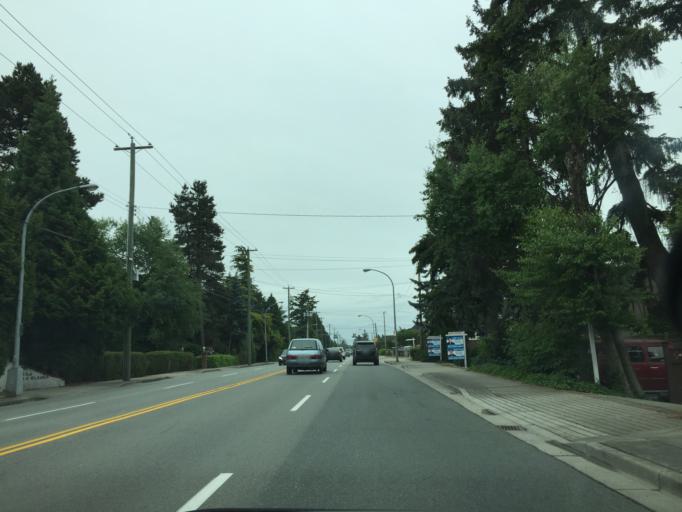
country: CA
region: British Columbia
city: Richmond
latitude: 49.1538
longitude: -123.1142
